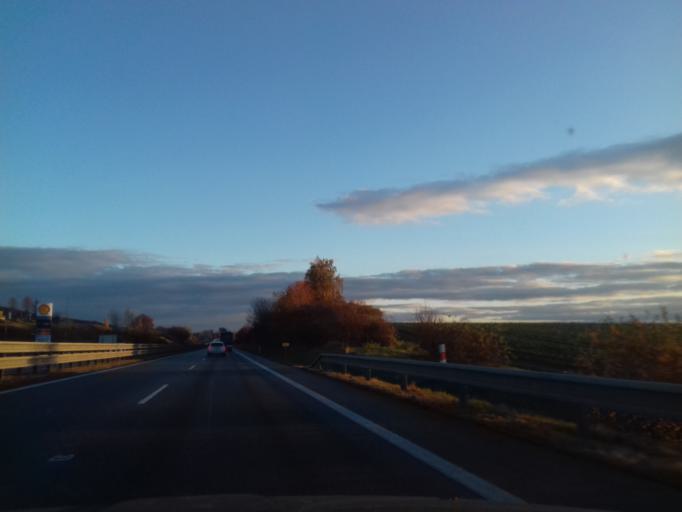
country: CZ
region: South Moravian
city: Pustimer
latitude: 49.3177
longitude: 17.0384
